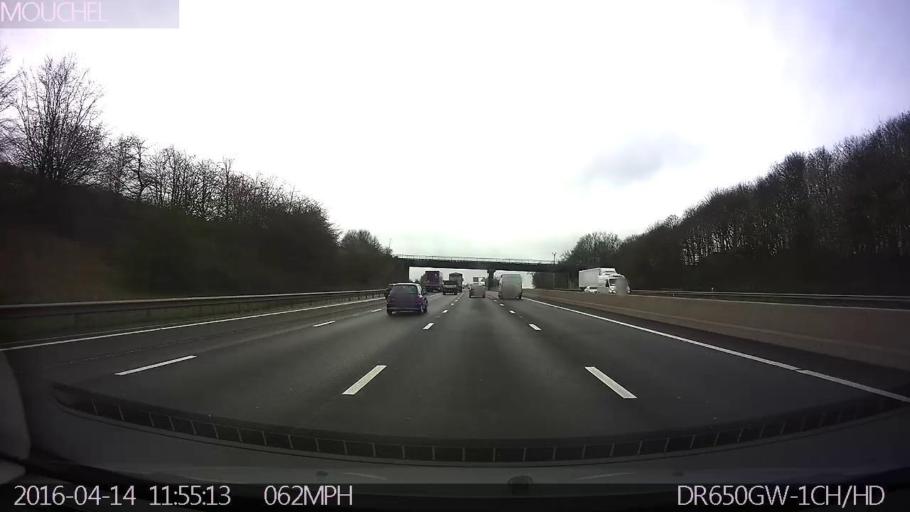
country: GB
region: England
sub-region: Derbyshire
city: Tibshelf
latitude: 53.1482
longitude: -1.3291
